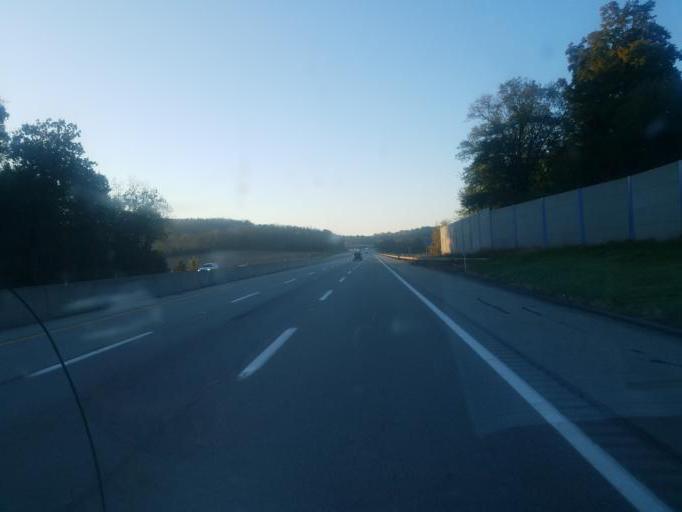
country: US
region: Pennsylvania
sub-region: Lawrence County
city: New Beaver
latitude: 40.8599
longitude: -80.3986
